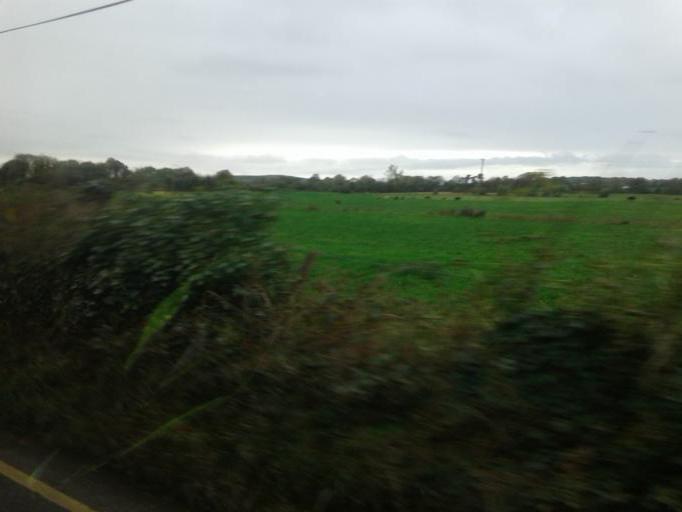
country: IE
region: Munster
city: Nenagh Bridge
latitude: 52.9301
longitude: -8.0431
